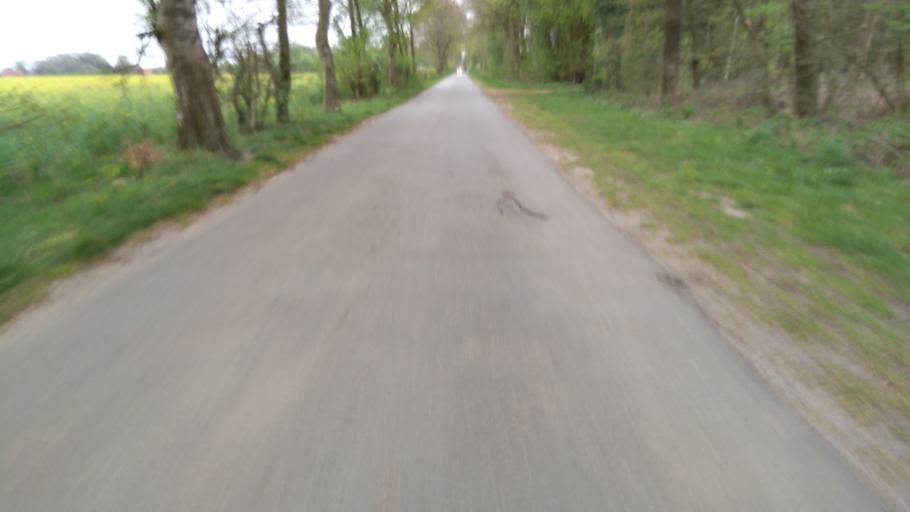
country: DE
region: Lower Saxony
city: Apensen
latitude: 53.4346
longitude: 9.5993
